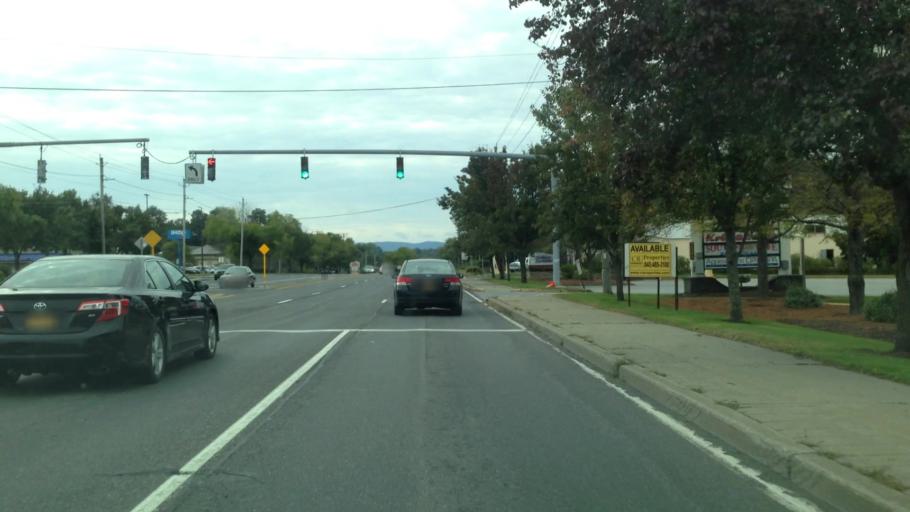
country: US
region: New York
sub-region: Dutchess County
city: Spackenkill
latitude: 41.6646
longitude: -73.9301
